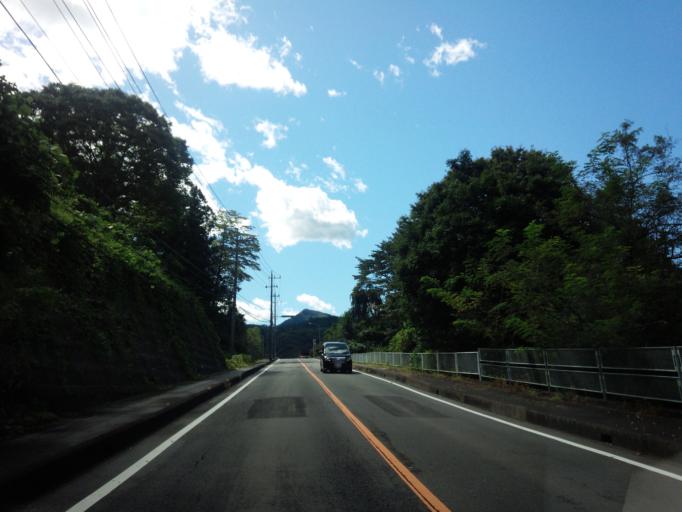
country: JP
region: Gunma
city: Nakanojomachi
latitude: 36.6129
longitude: 138.7962
